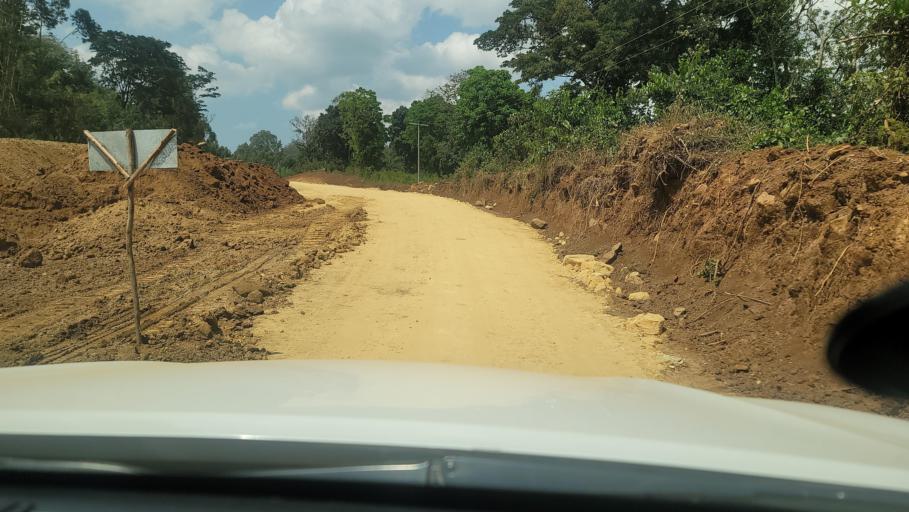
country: ET
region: Oromiya
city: Agaro
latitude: 7.7614
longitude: 36.2875
